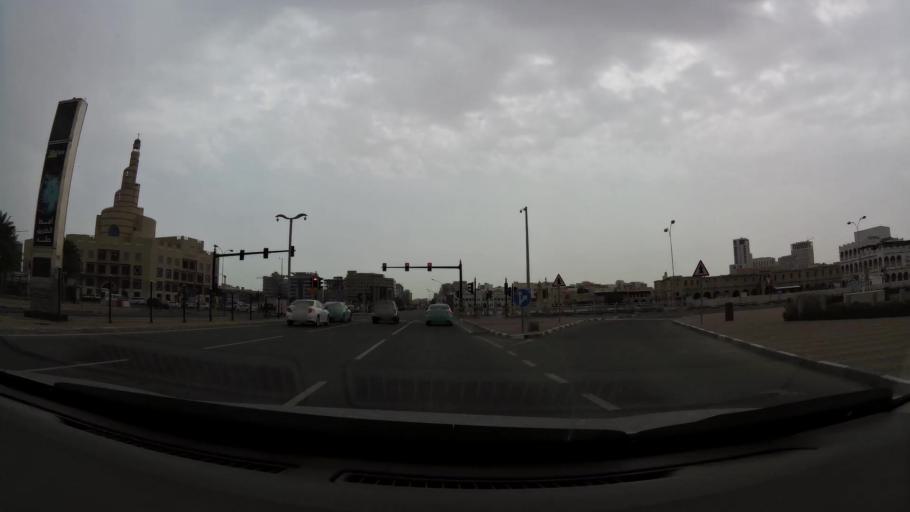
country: QA
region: Baladiyat ad Dawhah
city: Doha
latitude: 25.2902
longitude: 51.5344
